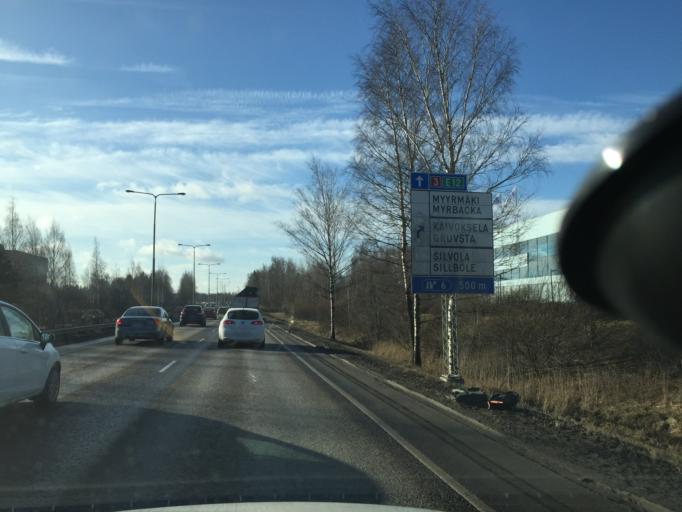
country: FI
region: Uusimaa
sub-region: Helsinki
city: Teekkarikylae
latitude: 60.2692
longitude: 24.8747
